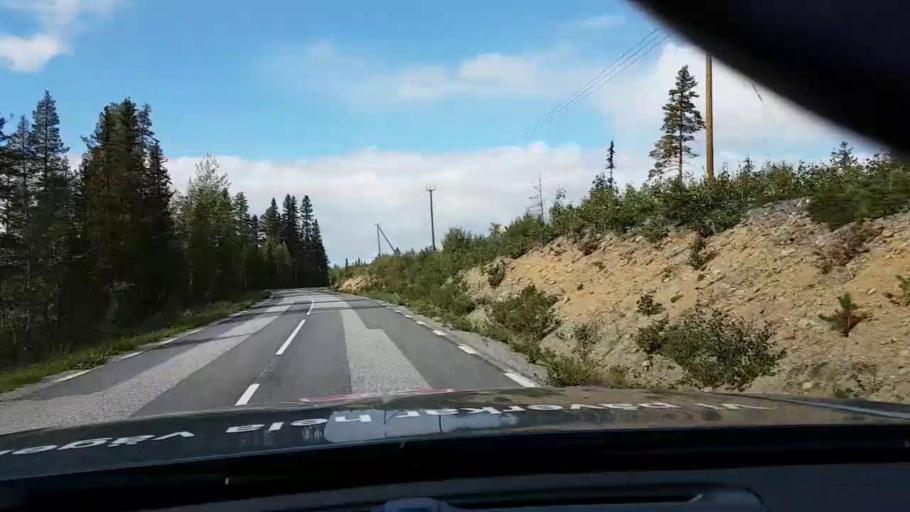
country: SE
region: Vaesterbotten
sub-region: Asele Kommun
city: Asele
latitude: 63.8259
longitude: 17.4752
